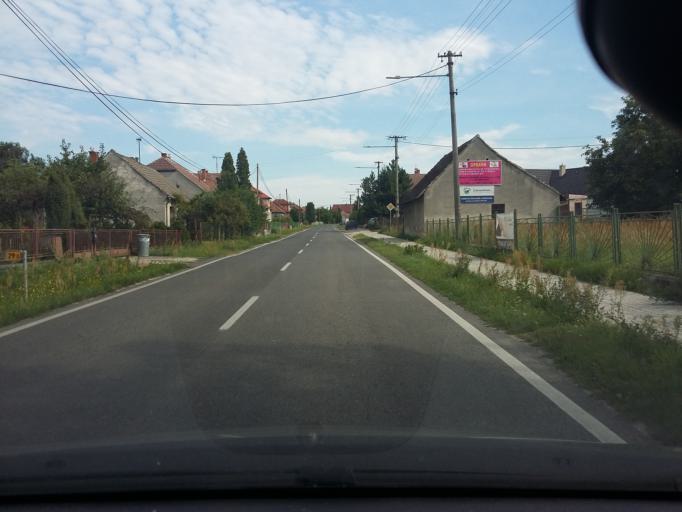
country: SK
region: Trnavsky
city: Gbely
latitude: 48.6348
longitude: 17.2032
